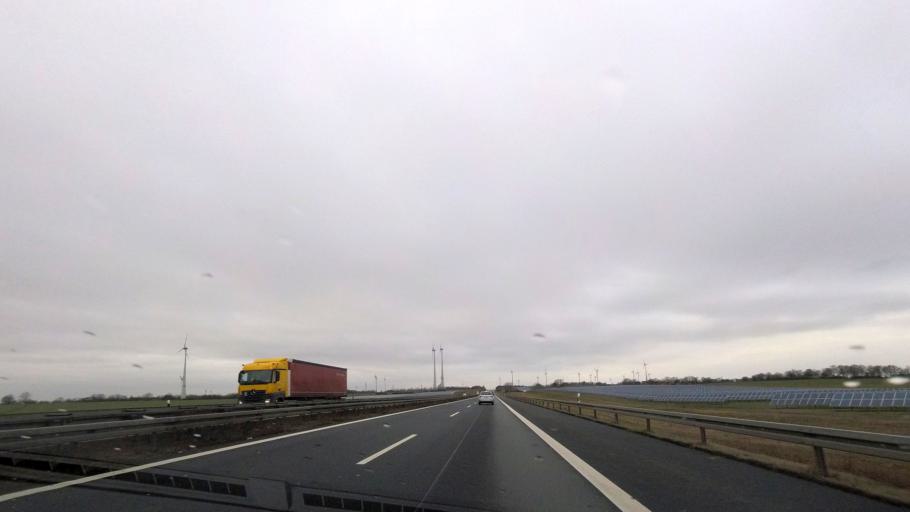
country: DE
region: Brandenburg
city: Gerdshagen
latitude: 53.2107
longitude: 12.2517
